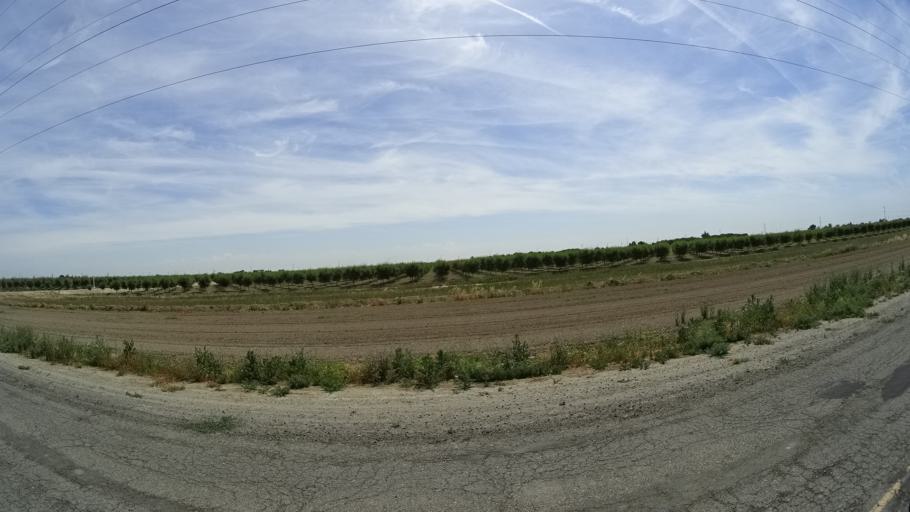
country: US
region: California
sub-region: Kings County
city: Hanford
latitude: 36.3459
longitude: -119.5920
